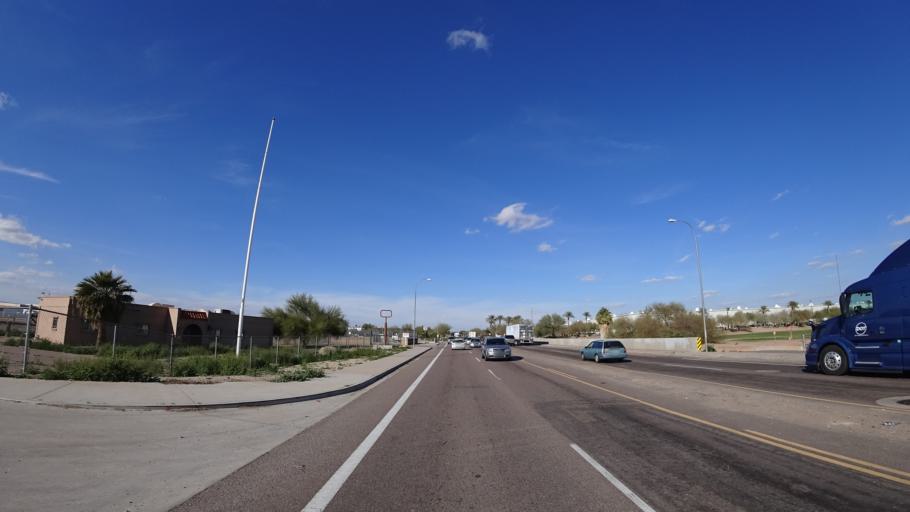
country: US
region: Arizona
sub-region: Maricopa County
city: Tolleson
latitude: 33.4449
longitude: -112.2213
